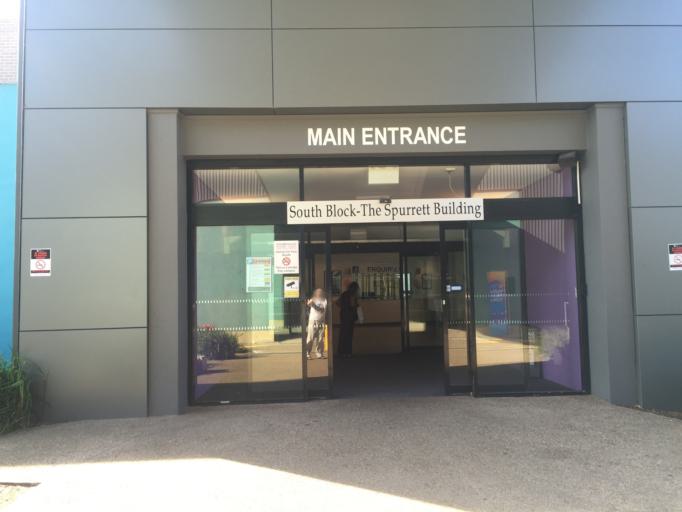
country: AU
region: New South Wales
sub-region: Penrith Municipality
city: Kingswood Park
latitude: -33.7606
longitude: 150.7130
